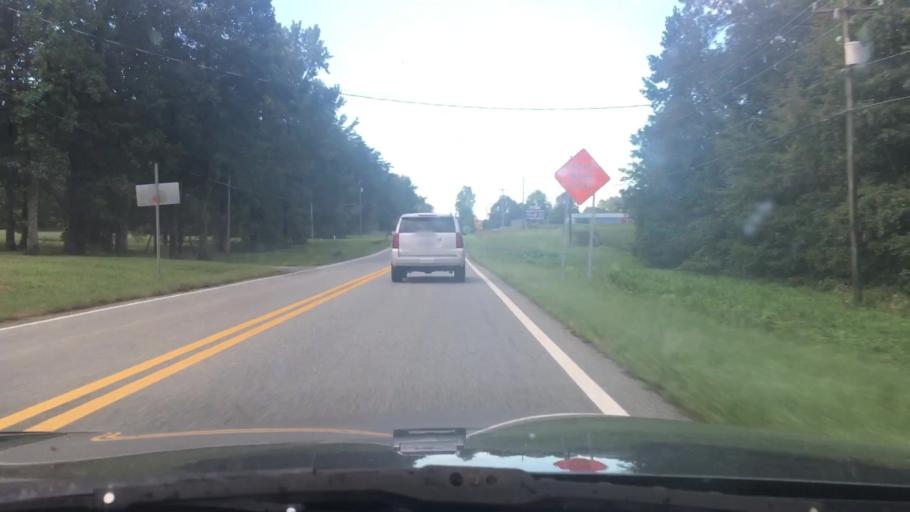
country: US
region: North Carolina
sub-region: Alamance County
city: Green Level
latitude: 36.1711
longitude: -79.3313
